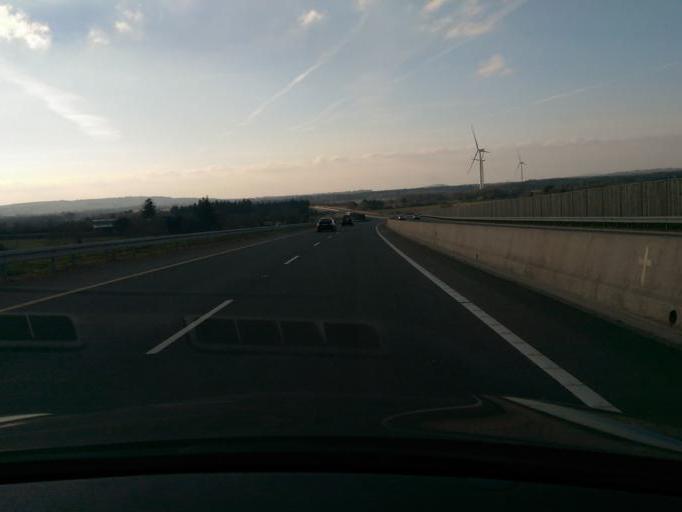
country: IE
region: Munster
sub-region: North Tipperary
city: Roscrea
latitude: 52.9181
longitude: -7.7198
